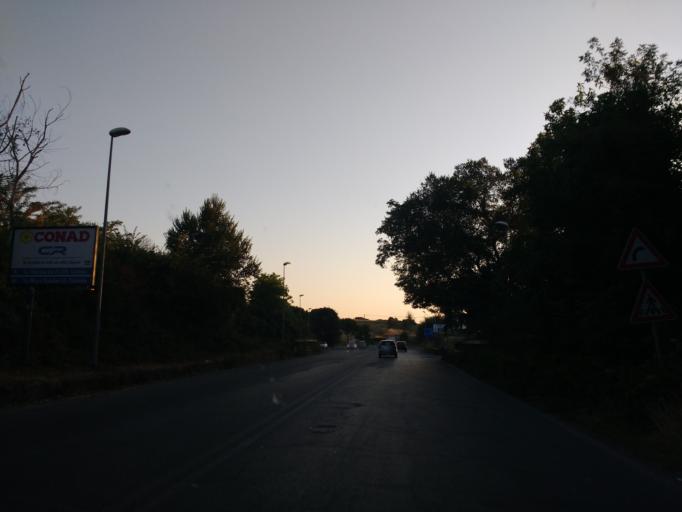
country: IT
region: Latium
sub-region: Citta metropolitana di Roma Capitale
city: Setteville
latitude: 41.9431
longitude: 12.6581
